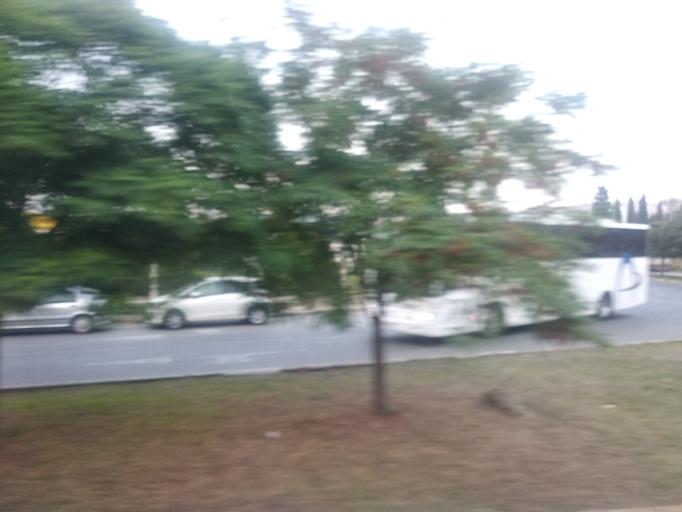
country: TR
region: Samsun
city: Samsun
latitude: 41.2862
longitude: 36.2882
